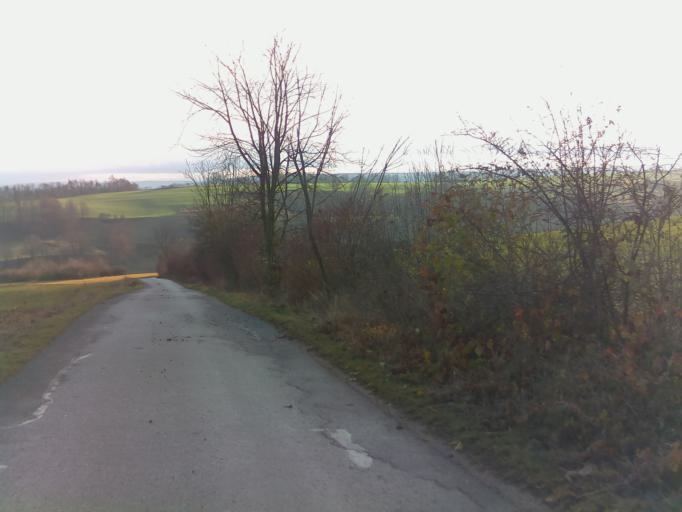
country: DE
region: Thuringia
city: Gumperda
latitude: 50.7948
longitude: 11.5146
